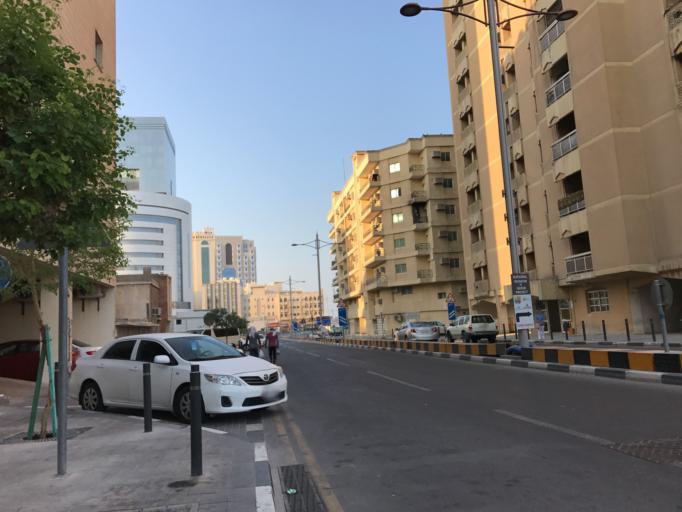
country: QA
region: Baladiyat ad Dawhah
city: Doha
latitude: 25.2848
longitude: 51.5476
